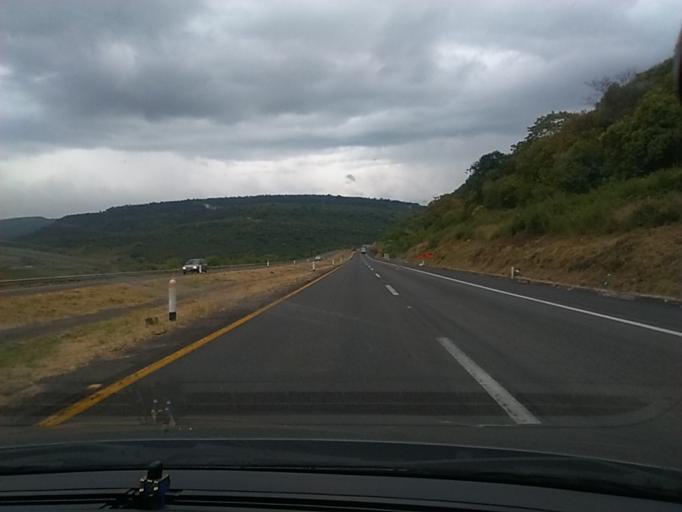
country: MX
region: Jalisco
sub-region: Zapotlan del Rey
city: Zapotlan del Rey
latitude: 20.5012
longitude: -102.9522
